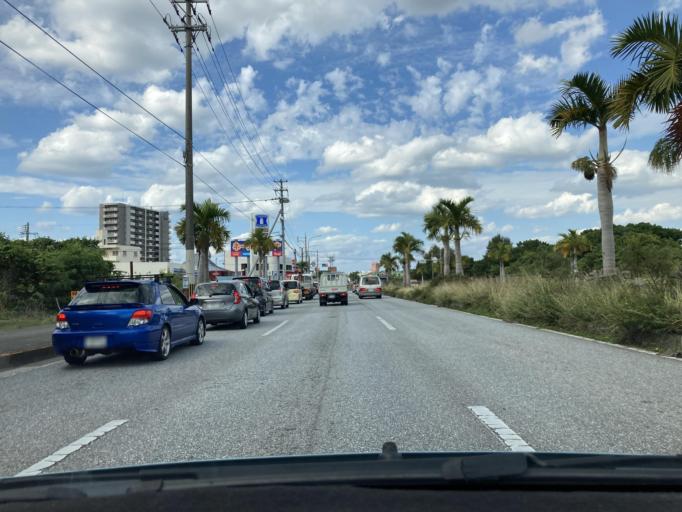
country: JP
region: Okinawa
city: Chatan
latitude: 26.3517
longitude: 127.7464
